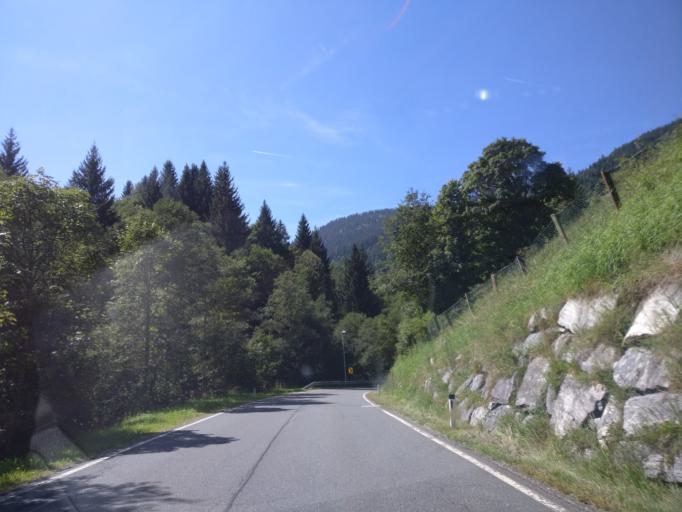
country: AT
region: Salzburg
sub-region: Politischer Bezirk Zell am See
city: Dienten am Hochkonig
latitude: 47.3866
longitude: 13.0102
